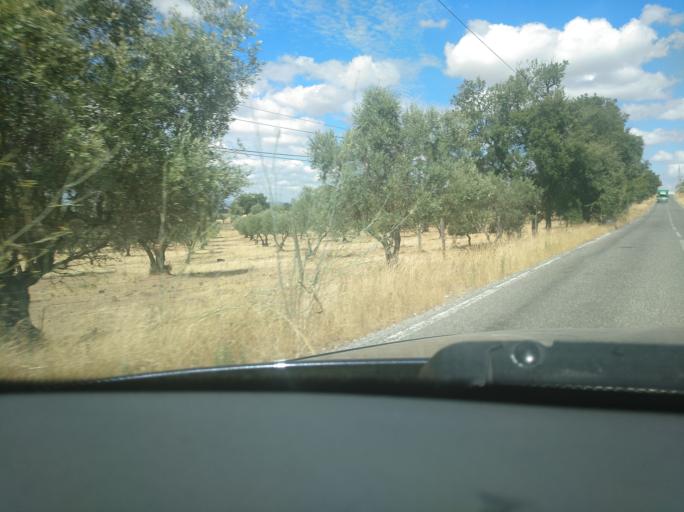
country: PT
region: Portalegre
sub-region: Arronches
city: Arronches
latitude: 39.0599
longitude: -7.4169
